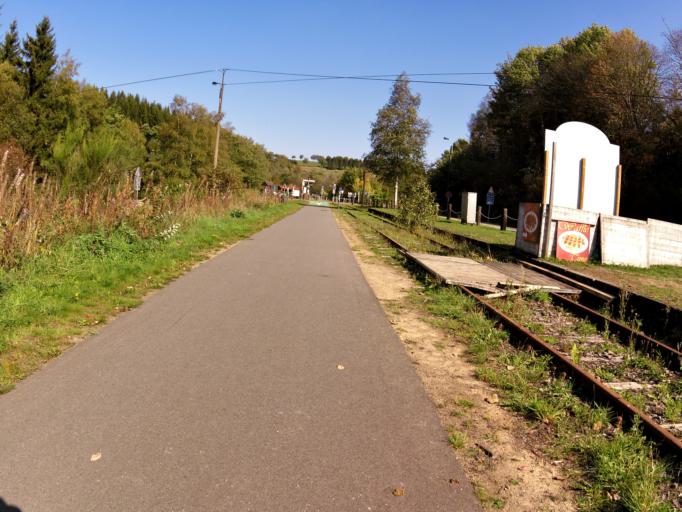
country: DE
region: North Rhine-Westphalia
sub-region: Regierungsbezirk Koln
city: Monschau
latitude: 50.5205
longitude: 6.2060
